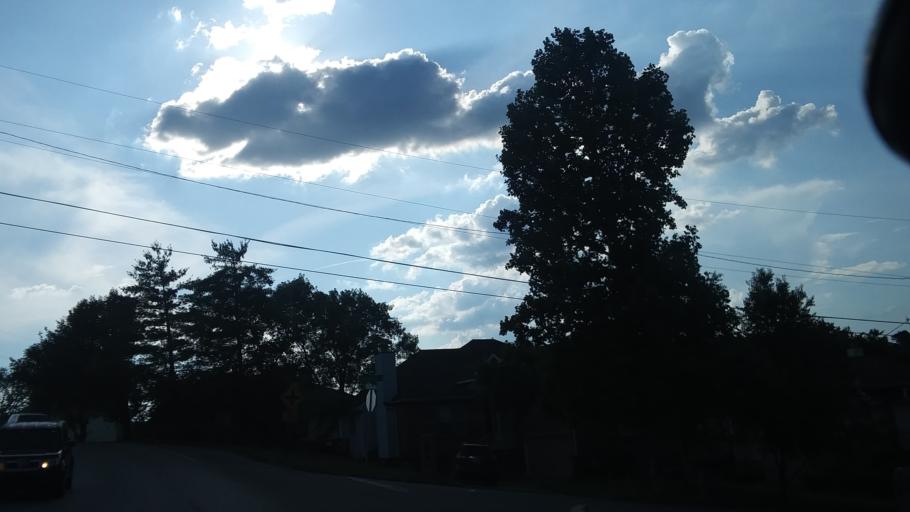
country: US
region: Tennessee
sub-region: Rutherford County
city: La Vergne
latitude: 36.0778
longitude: -86.6666
